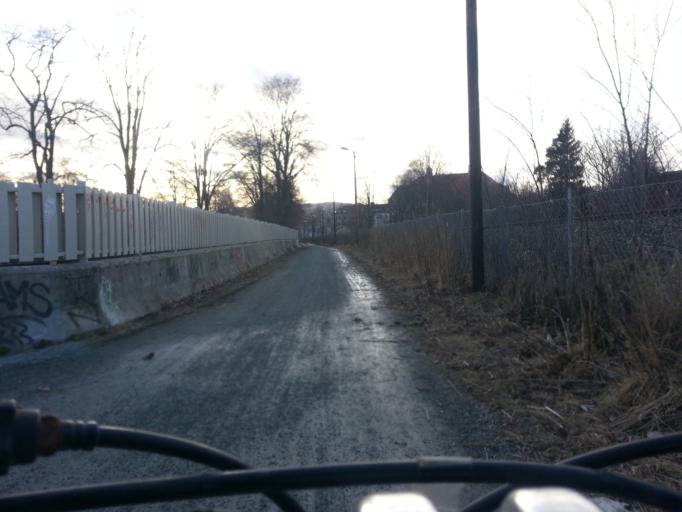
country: NO
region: Sor-Trondelag
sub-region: Trondheim
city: Trondheim
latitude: 63.4406
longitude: 10.4390
